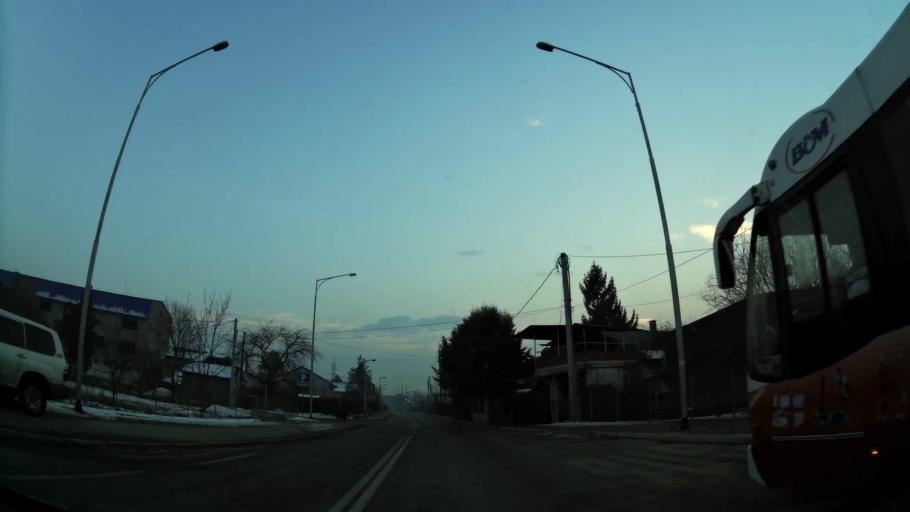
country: MK
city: Creshevo
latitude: 42.0015
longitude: 21.5024
